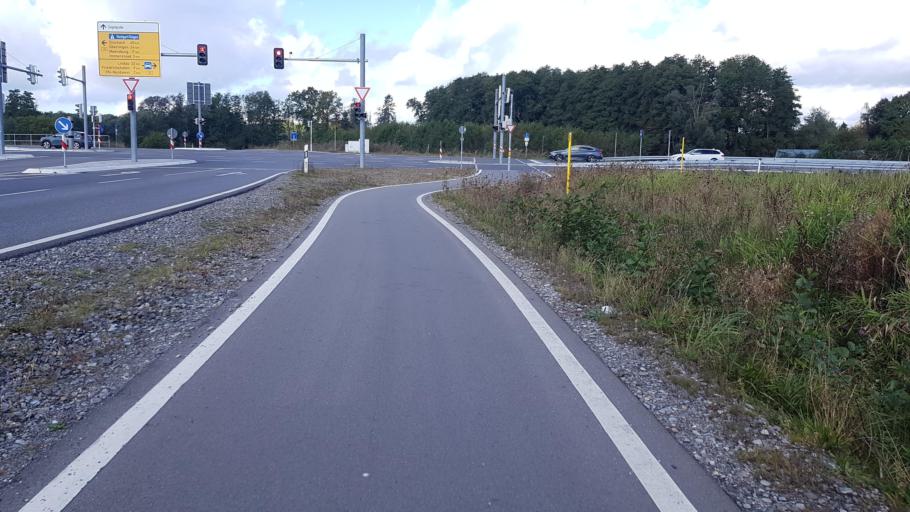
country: DE
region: Baden-Wuerttemberg
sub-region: Tuebingen Region
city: Immenstaad am Bodensee
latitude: 47.6731
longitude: 9.3949
